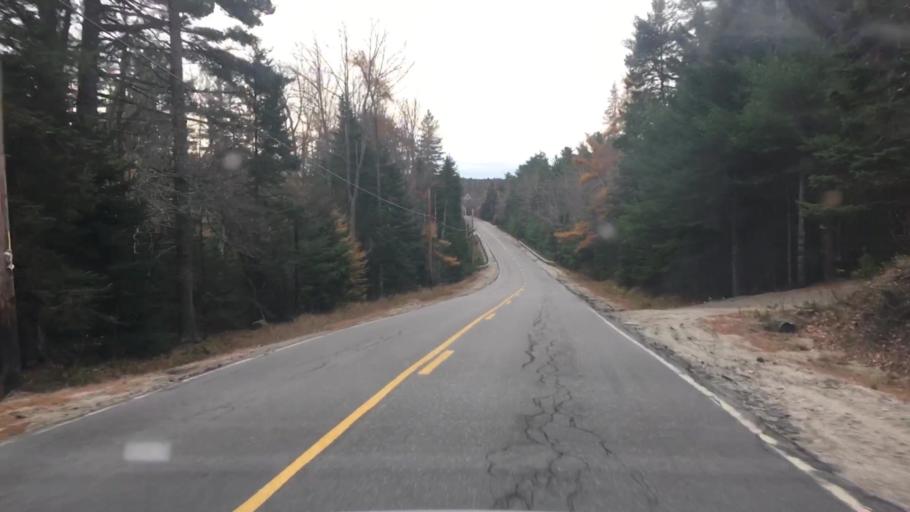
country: US
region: Maine
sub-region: Hancock County
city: Penobscot
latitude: 44.4275
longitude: -68.6249
